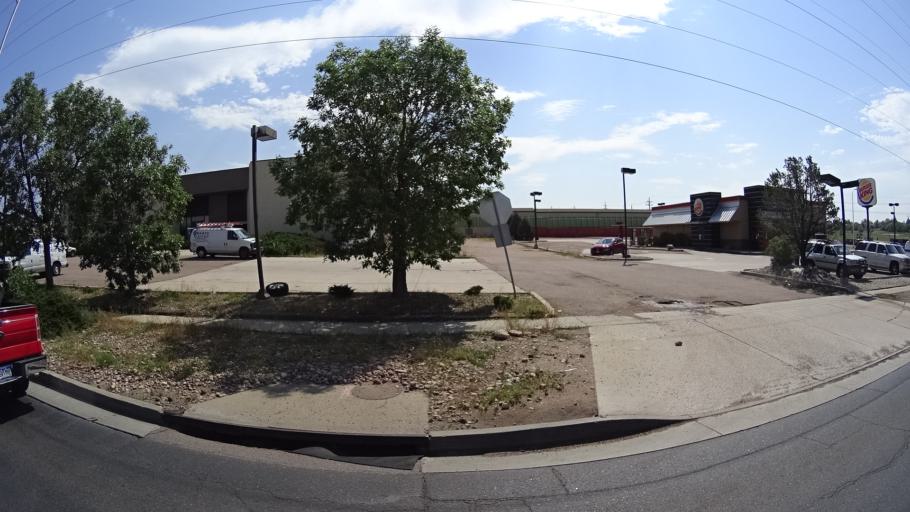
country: US
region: Colorado
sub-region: El Paso County
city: Stratmoor
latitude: 38.8261
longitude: -104.7574
